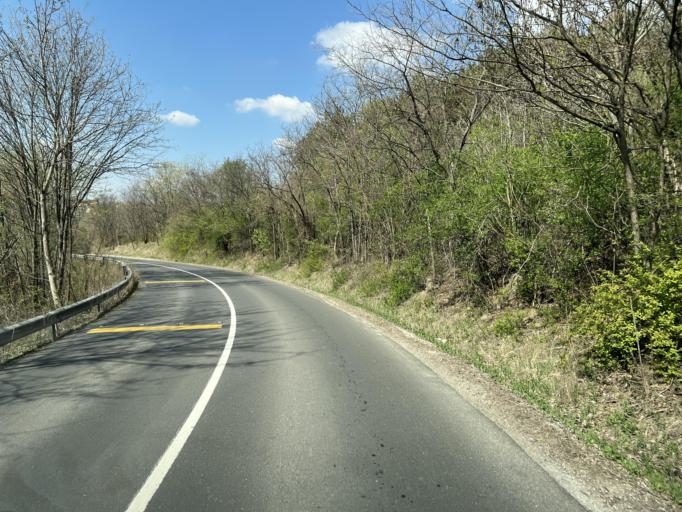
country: HU
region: Pest
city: Galgamacsa
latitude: 47.6784
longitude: 19.3755
